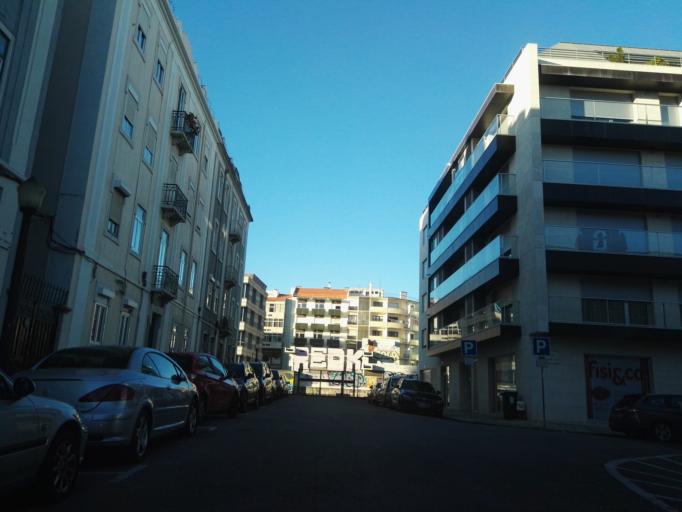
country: PT
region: Lisbon
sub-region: Lisbon
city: Lisbon
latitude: 38.7444
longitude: -9.1460
